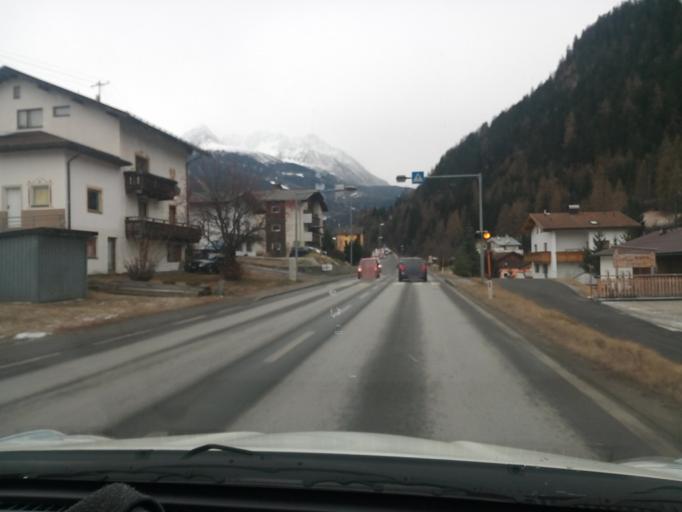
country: AT
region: Tyrol
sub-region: Politischer Bezirk Landeck
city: Nauders
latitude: 46.8894
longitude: 10.4999
